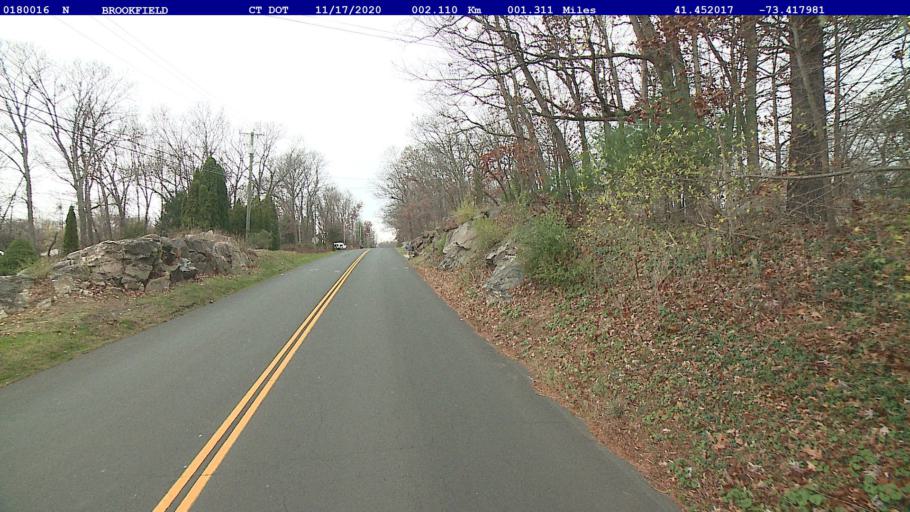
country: US
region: Connecticut
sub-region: Fairfield County
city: Danbury
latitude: 41.4520
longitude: -73.4180
